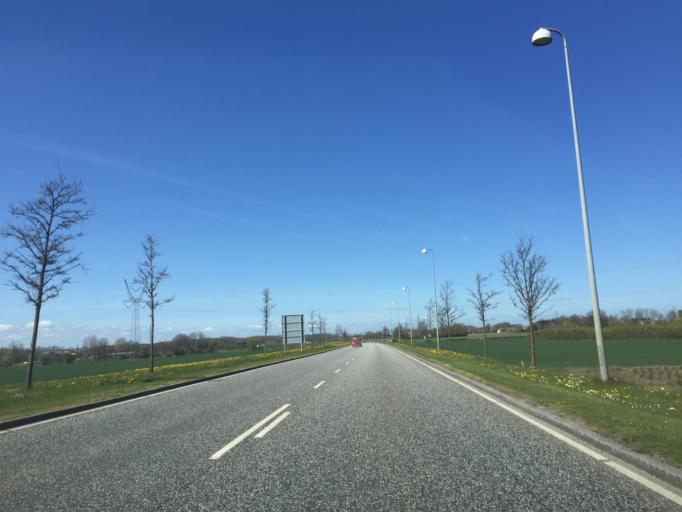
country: DK
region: South Denmark
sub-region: Odense Kommune
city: Neder Holluf
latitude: 55.3671
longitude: 10.5149
